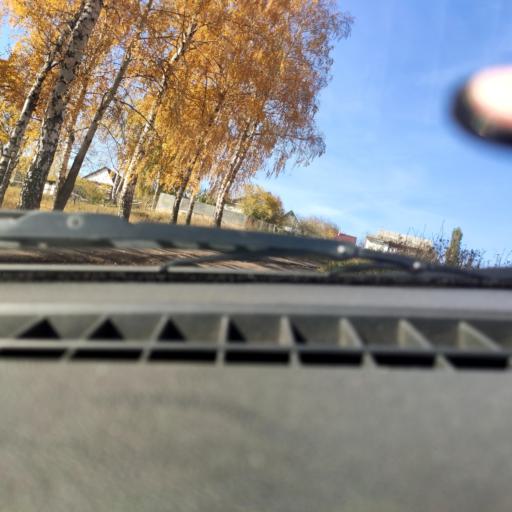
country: RU
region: Bashkortostan
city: Ufa
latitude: 54.8400
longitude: 56.1594
